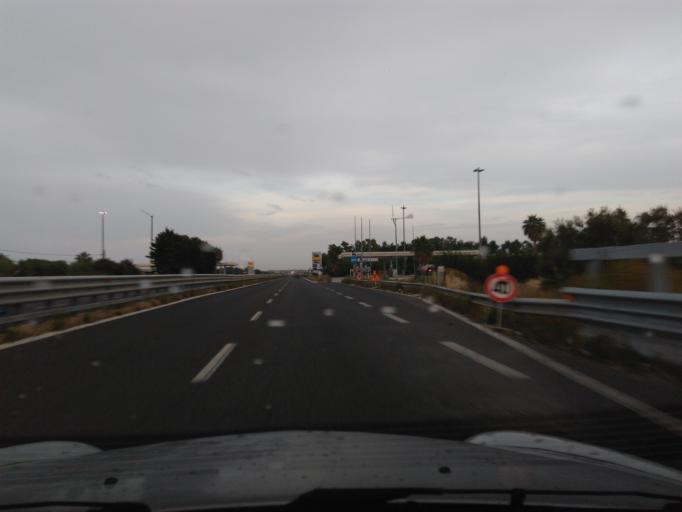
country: IT
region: Apulia
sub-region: Provincia di Bari
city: Giovinazzo
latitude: 41.1682
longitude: 16.7022
